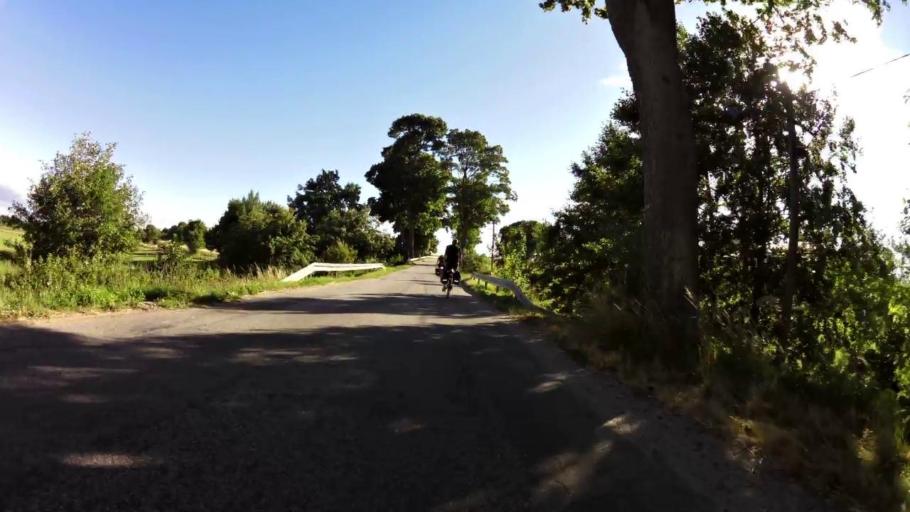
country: PL
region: West Pomeranian Voivodeship
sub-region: Powiat swidwinski
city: Swidwin
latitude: 53.7720
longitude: 15.7384
